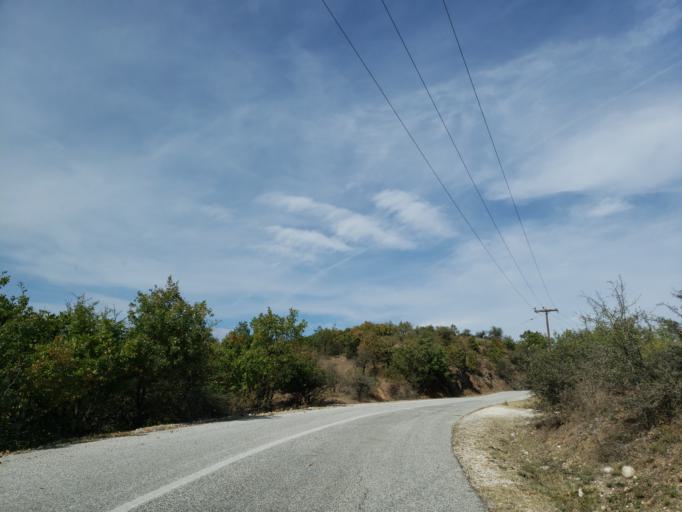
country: GR
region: Thessaly
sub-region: Trikala
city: Kastraki
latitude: 39.7340
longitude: 21.6550
